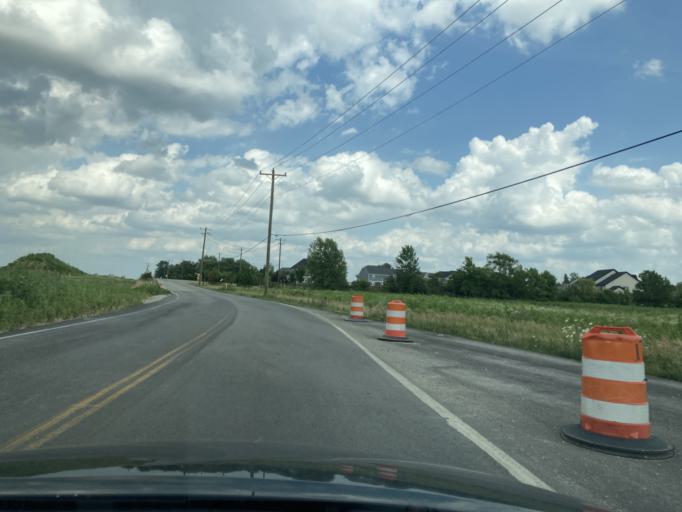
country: US
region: Indiana
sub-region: Boone County
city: Zionsville
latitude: 39.9989
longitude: -86.2184
